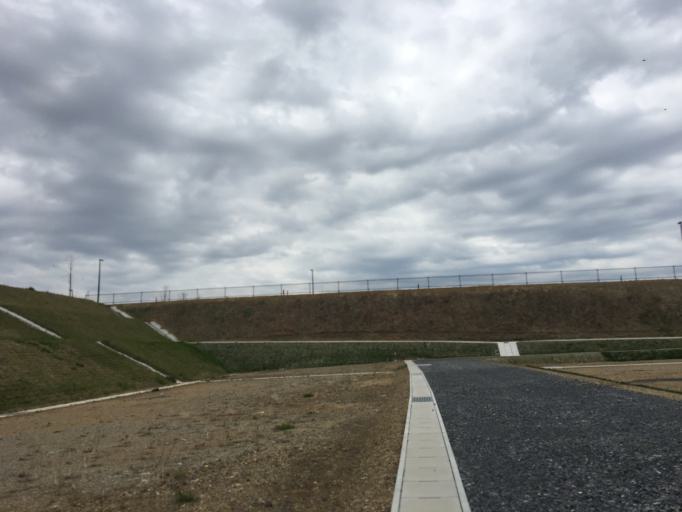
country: JP
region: Iwate
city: Ofunato
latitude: 39.0156
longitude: 141.6246
